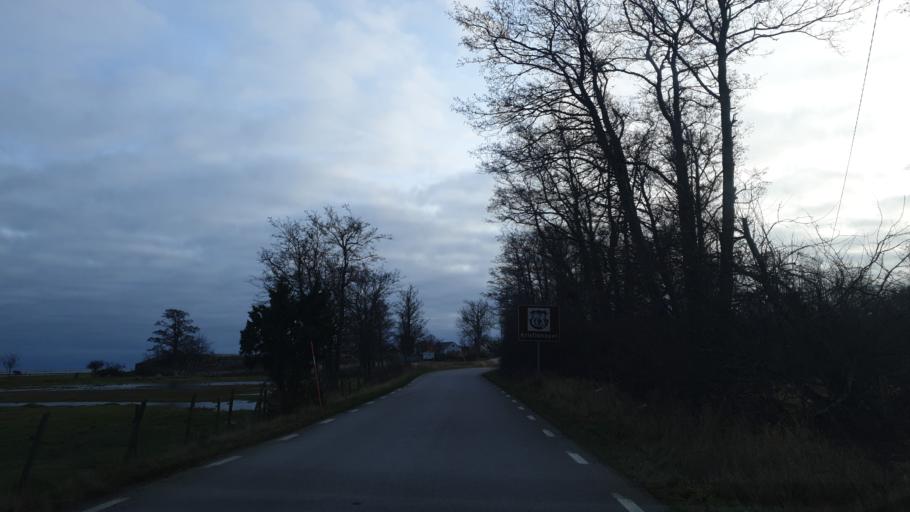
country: SE
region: Kalmar
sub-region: Torsas Kommun
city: Torsas
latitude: 56.2619
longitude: 16.0391
